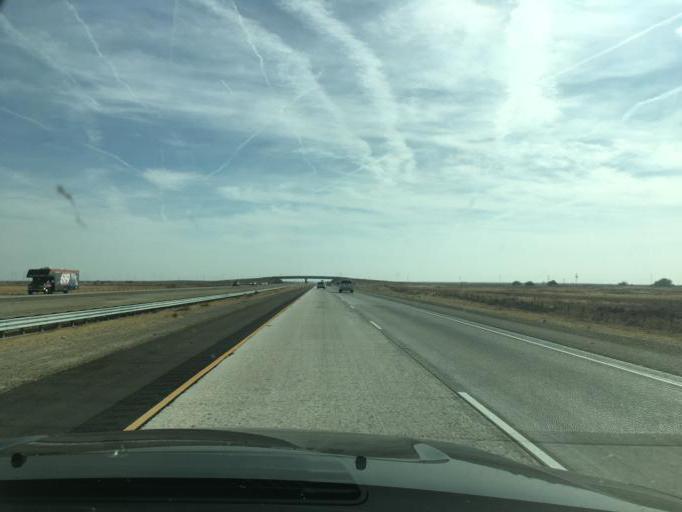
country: US
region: California
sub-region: Kern County
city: Lost Hills
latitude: 35.5633
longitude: -119.6039
